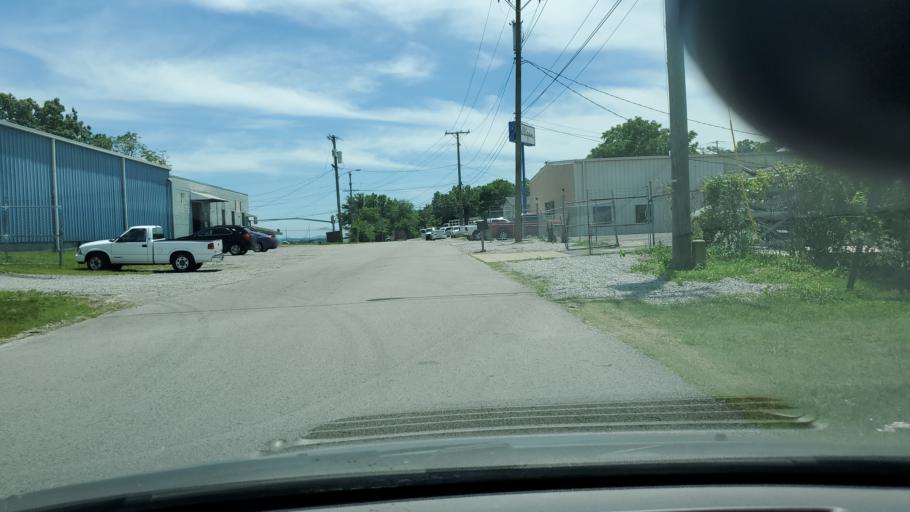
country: US
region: Tennessee
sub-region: Davidson County
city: Nashville
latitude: 36.2061
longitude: -86.7510
